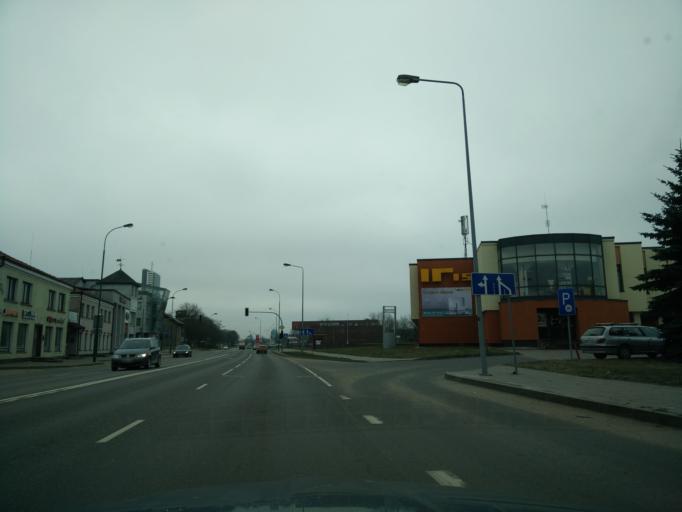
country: LT
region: Klaipedos apskritis
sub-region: Klaipeda
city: Klaipeda
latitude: 55.6969
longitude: 21.1377
